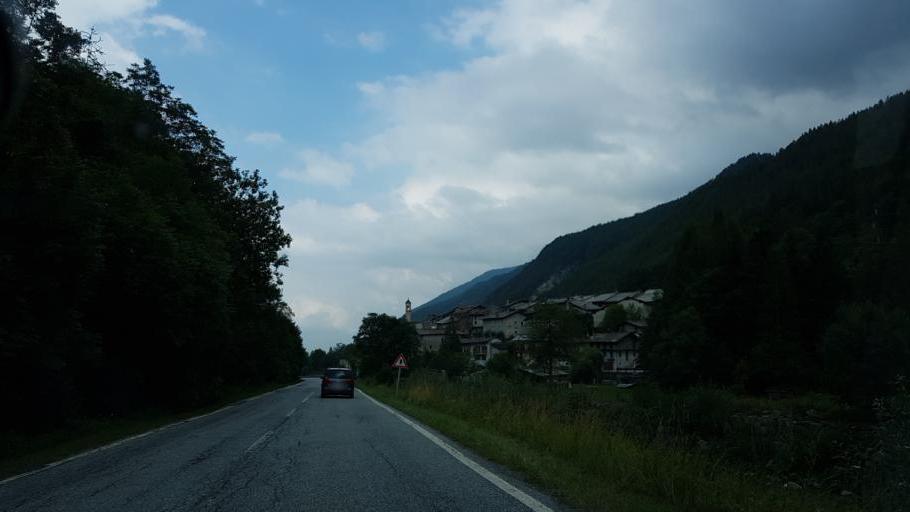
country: IT
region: Piedmont
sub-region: Provincia di Cuneo
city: Casteldelfino
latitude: 44.5835
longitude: 7.0964
